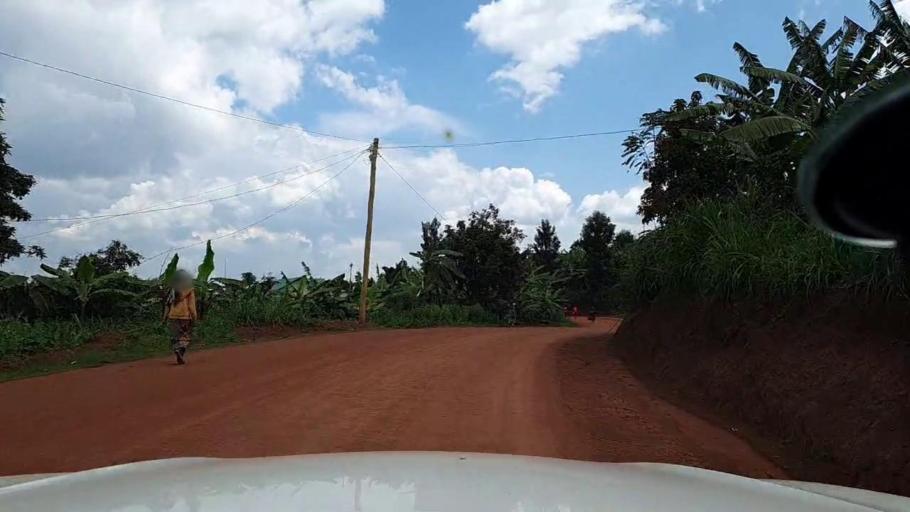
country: RW
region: Kigali
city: Kigali
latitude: -1.8100
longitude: 29.8442
